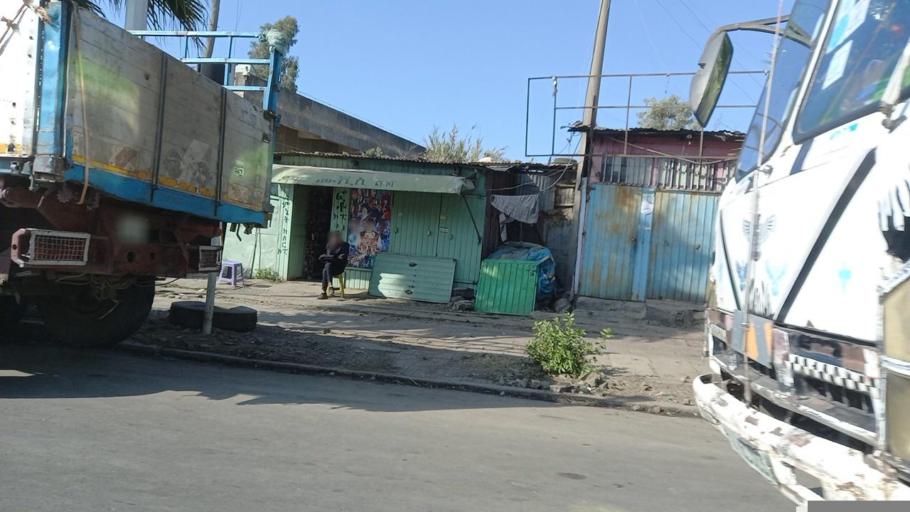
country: ET
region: Adis Abeba
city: Addis Ababa
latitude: 8.9444
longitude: 38.7664
